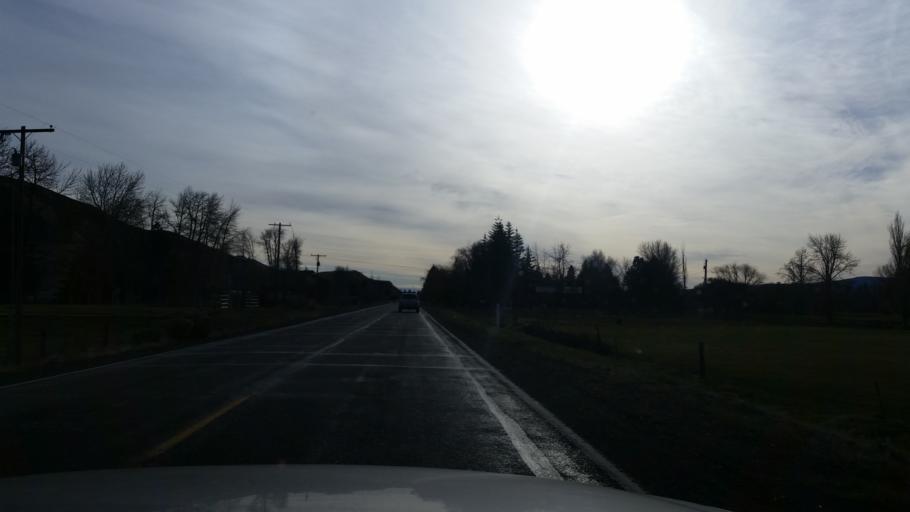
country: US
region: Washington
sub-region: Kittitas County
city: Ellensburg
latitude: 47.0876
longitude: -120.6796
